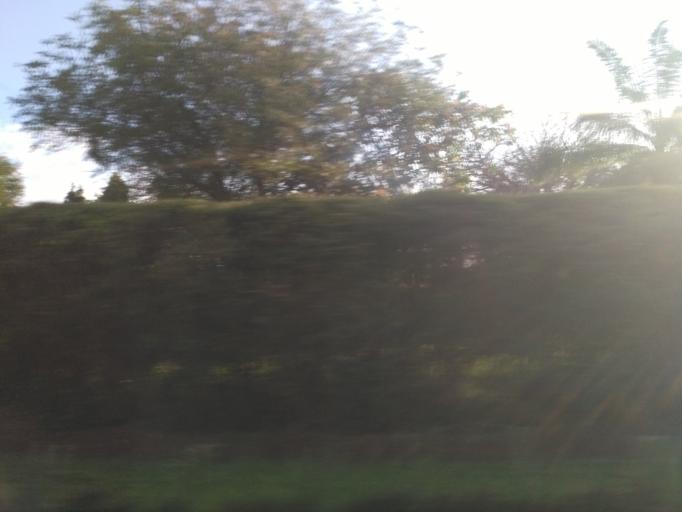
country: TZ
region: Dar es Salaam
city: Magomeni
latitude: -6.7821
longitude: 39.2733
